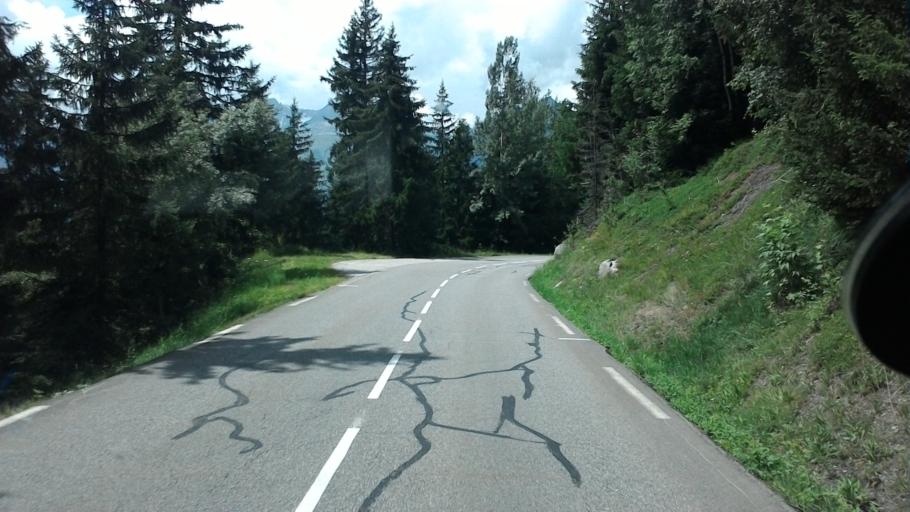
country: FR
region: Rhone-Alpes
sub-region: Departement de la Savoie
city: Seez
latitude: 45.6207
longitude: 6.8421
